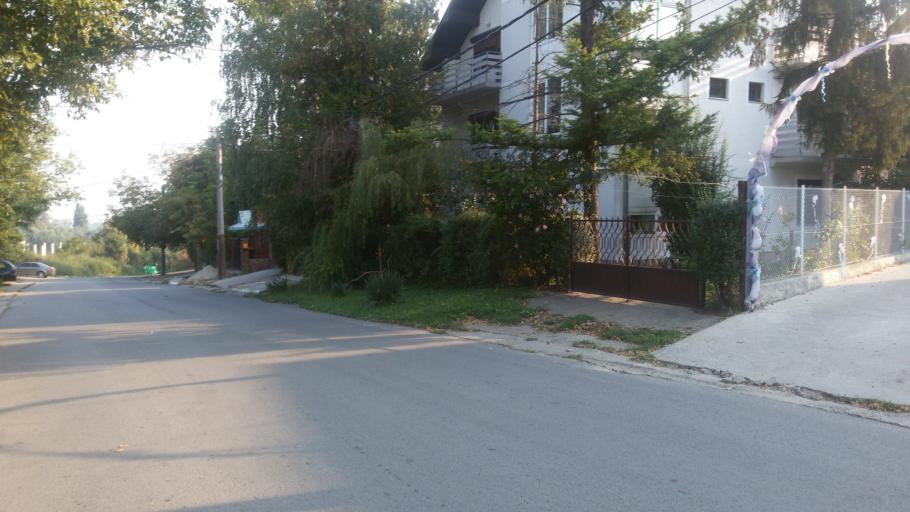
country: RS
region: Central Serbia
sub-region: Belgrade
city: Cukarica
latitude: 44.7474
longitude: 20.3994
